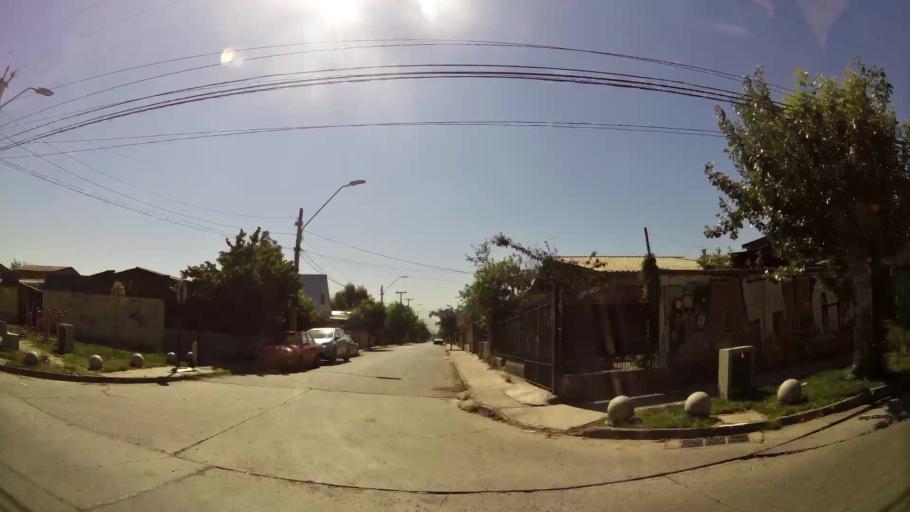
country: CL
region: Santiago Metropolitan
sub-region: Provincia de Santiago
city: La Pintana
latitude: -33.5531
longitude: -70.6540
